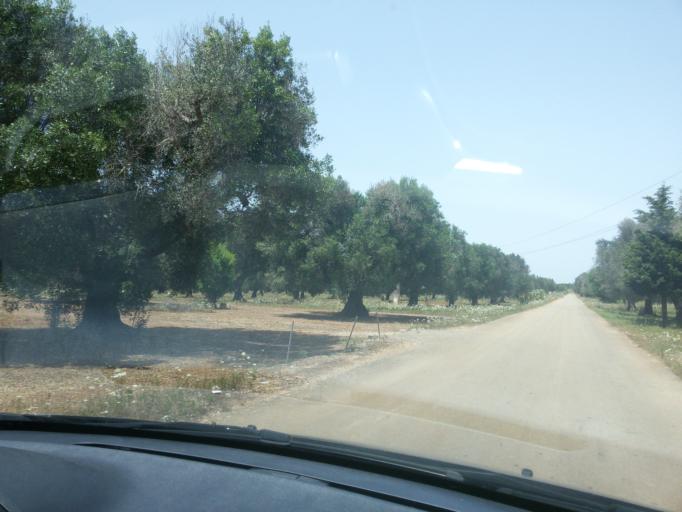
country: IT
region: Apulia
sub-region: Provincia di Lecce
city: Porto Cesareo
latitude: 40.3200
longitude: 17.8942
